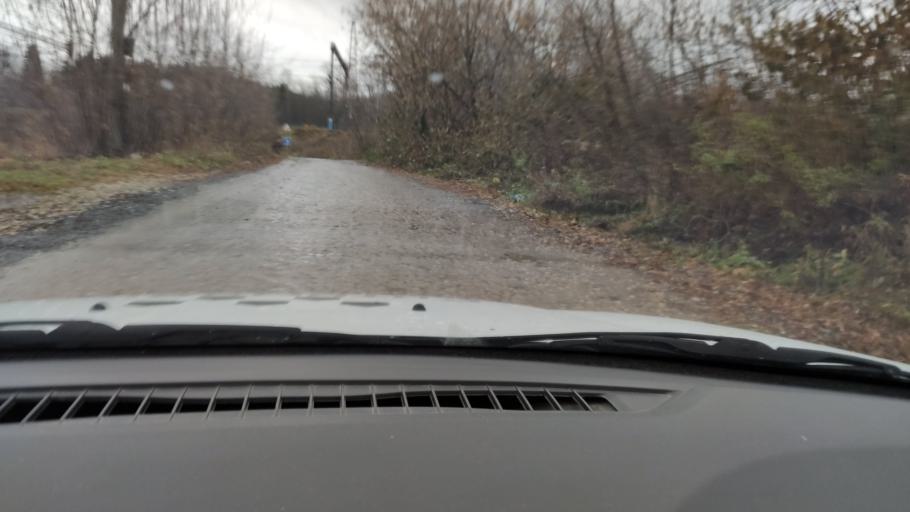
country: RU
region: Perm
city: Sylva
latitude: 58.0440
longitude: 56.7467
